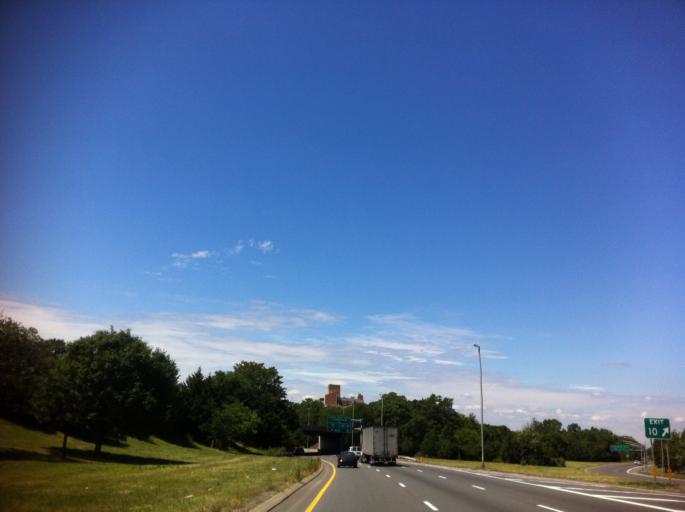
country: US
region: New York
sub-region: Bronx
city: The Bronx
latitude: 40.8195
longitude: -73.8106
